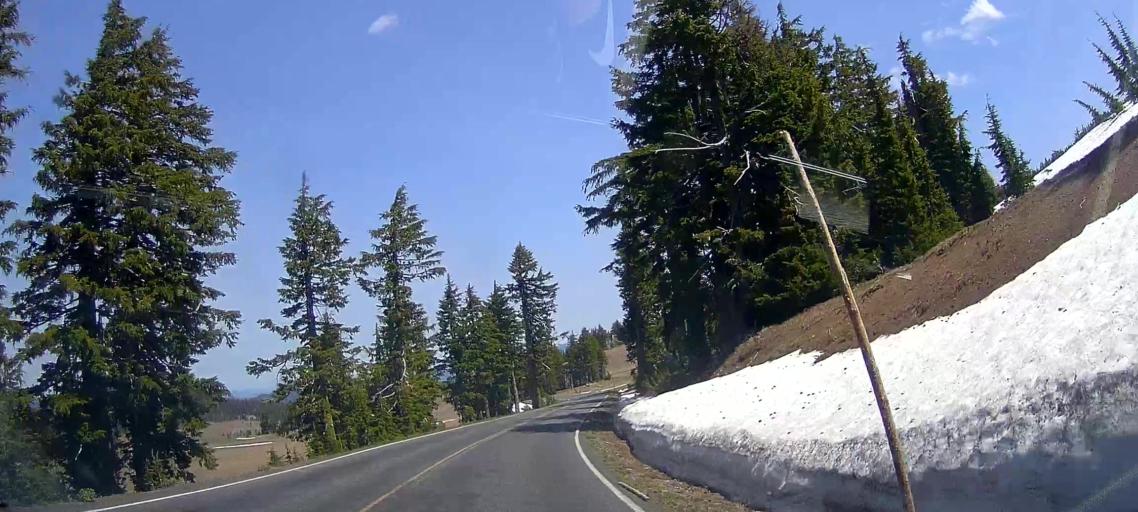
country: US
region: Oregon
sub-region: Jackson County
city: Shady Cove
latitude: 42.9729
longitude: -122.1529
